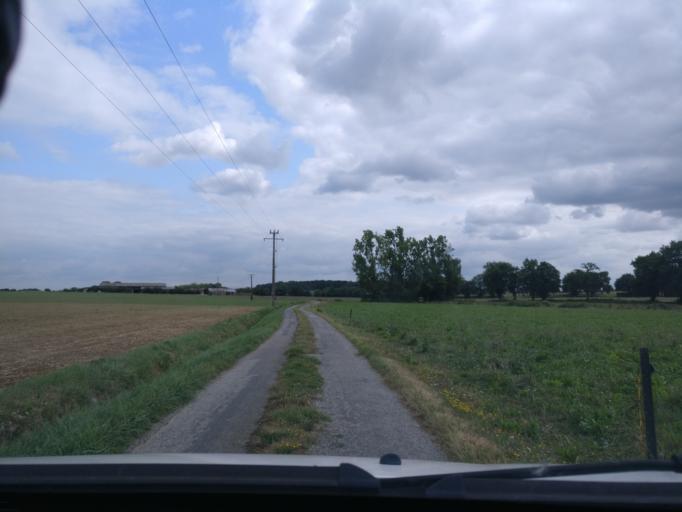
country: FR
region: Brittany
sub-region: Departement d'Ille-et-Vilaine
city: Nouvoitou
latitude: 48.0709
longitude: -1.5606
